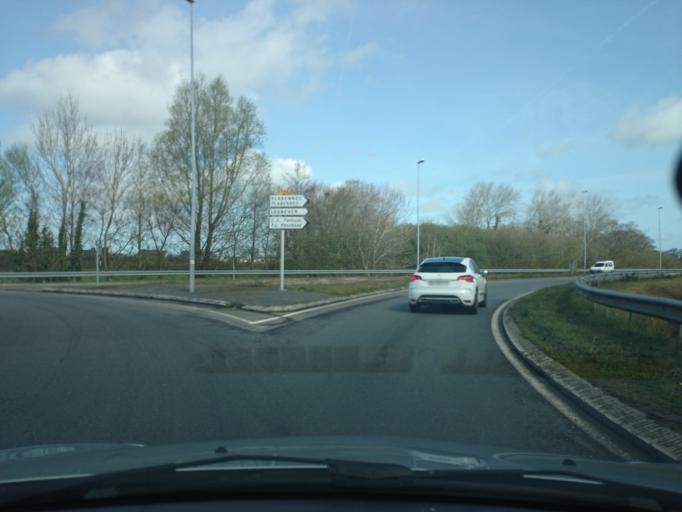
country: FR
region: Brittany
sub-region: Departement du Finistere
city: Gouesnou
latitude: 48.4439
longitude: -4.4562
